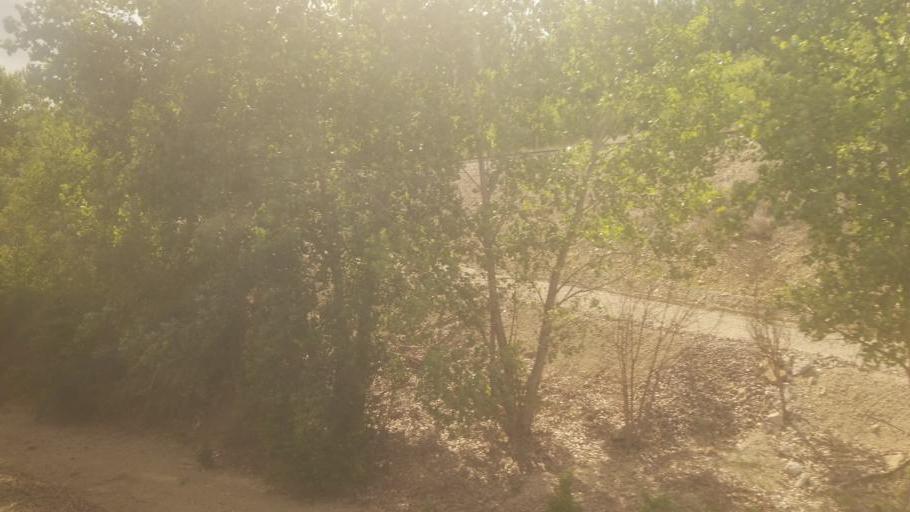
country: US
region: Kansas
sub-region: Johnson County
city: Westwood
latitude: 39.0776
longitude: -94.6163
